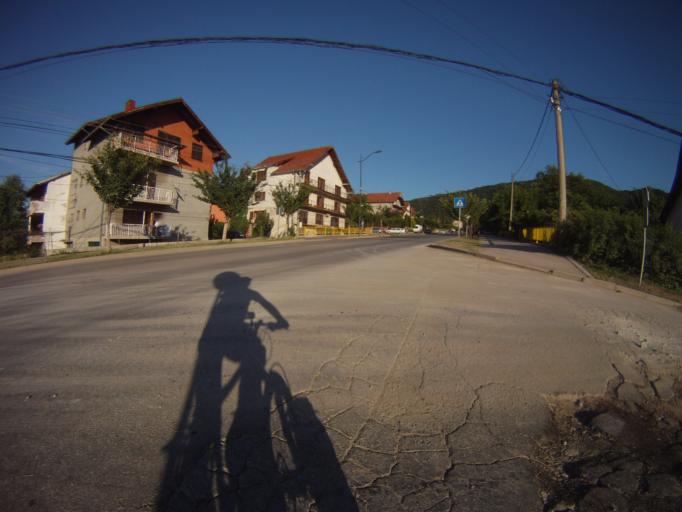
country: RS
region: Central Serbia
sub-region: Nisavski Okrug
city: Niska Banja
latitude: 43.2966
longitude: 22.0023
